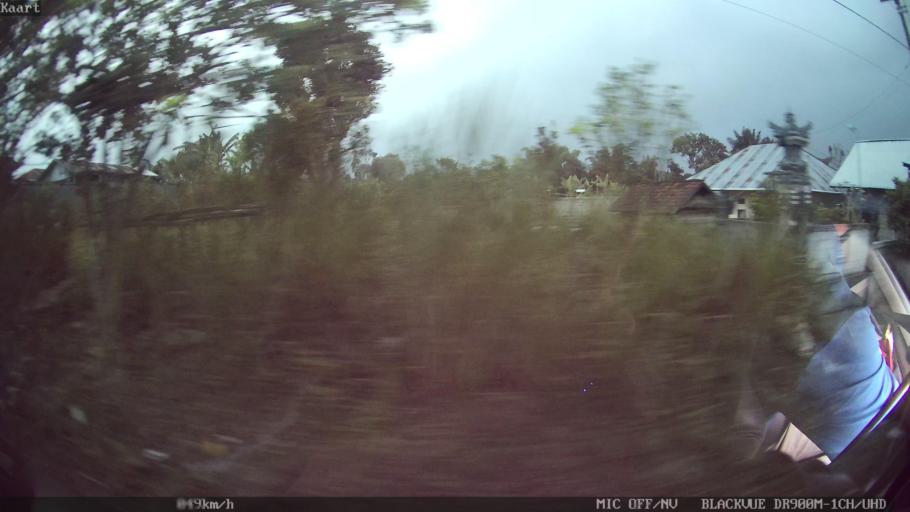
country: ID
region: Bali
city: Banjar Kedisan
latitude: -8.2773
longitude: 115.3245
